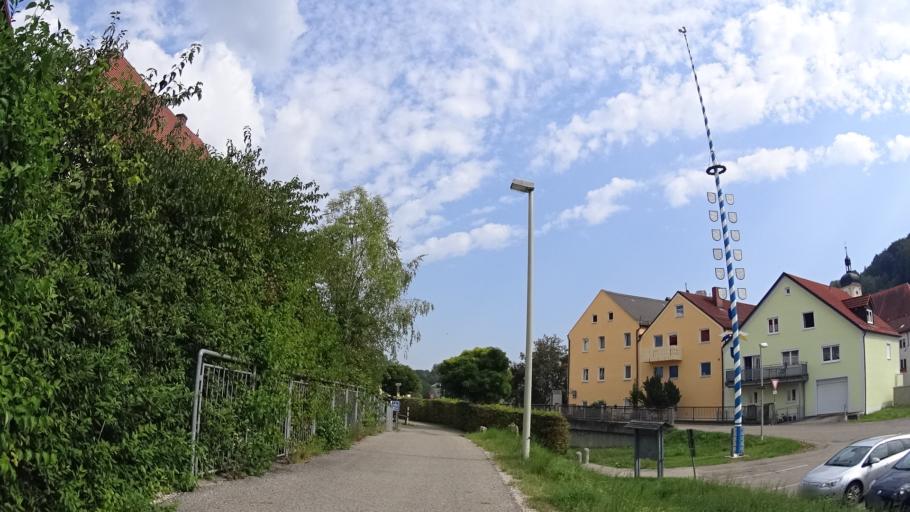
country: DE
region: Bavaria
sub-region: Upper Bavaria
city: Mindelstetten
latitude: 48.8974
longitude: 11.6490
